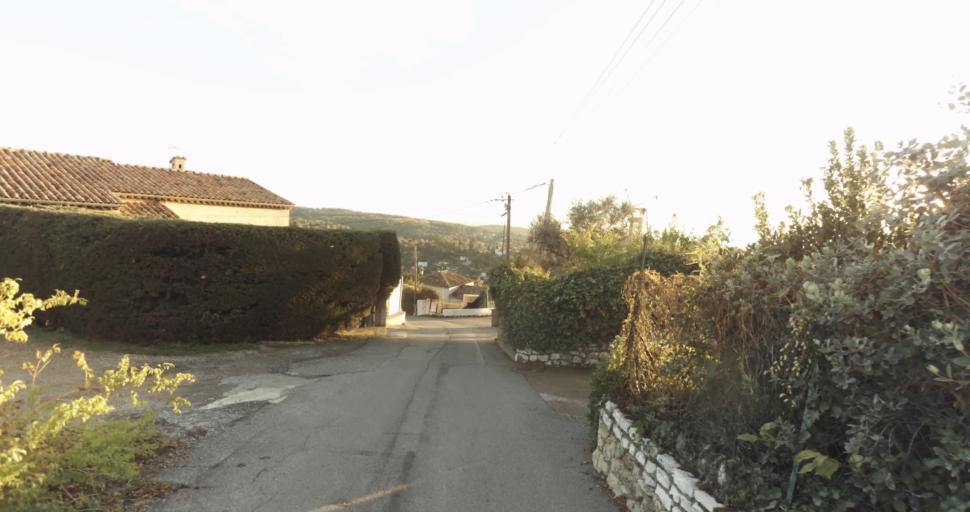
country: FR
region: Provence-Alpes-Cote d'Azur
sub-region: Departement des Alpes-Maritimes
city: Vence
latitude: 43.7276
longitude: 7.0926
